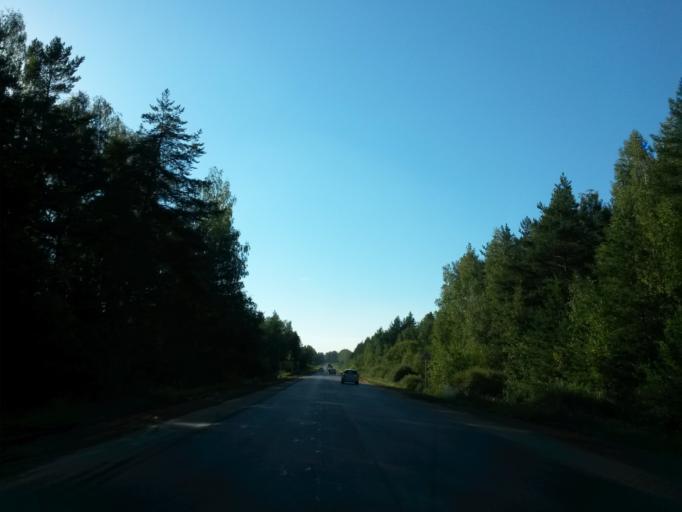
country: RU
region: Ivanovo
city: Novo-Talitsy
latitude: 57.0214
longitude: 40.7719
